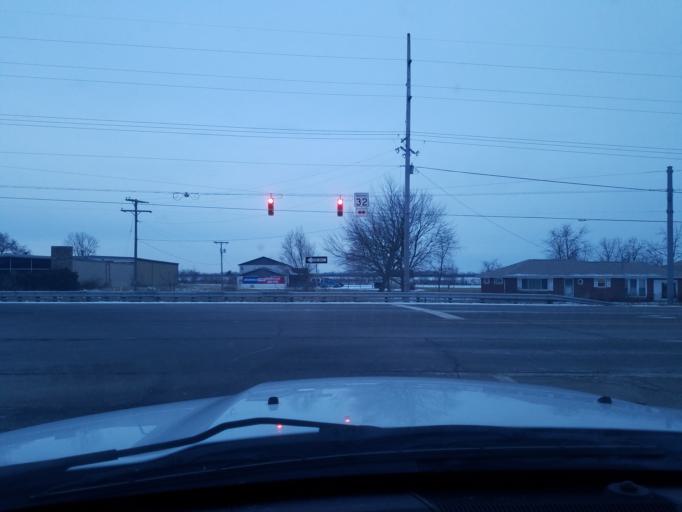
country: US
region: Indiana
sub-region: Delaware County
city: Muncie
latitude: 40.1931
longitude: -85.3383
